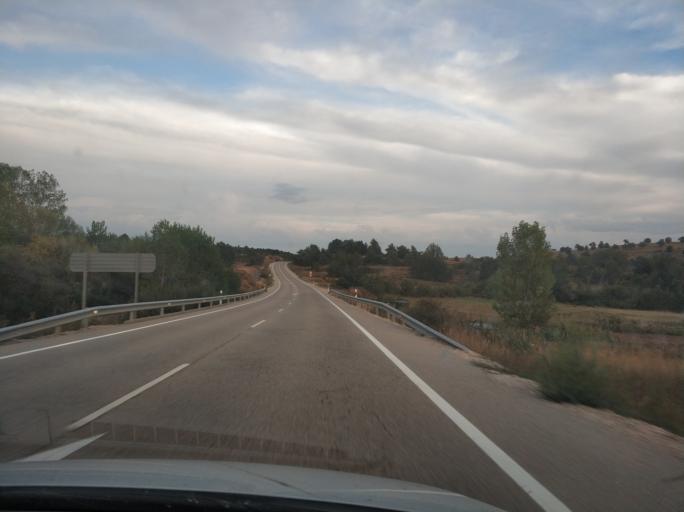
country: ES
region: Castille and Leon
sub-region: Provincia de Burgos
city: Cabezon de la Sierra
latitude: 41.8959
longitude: -3.2625
